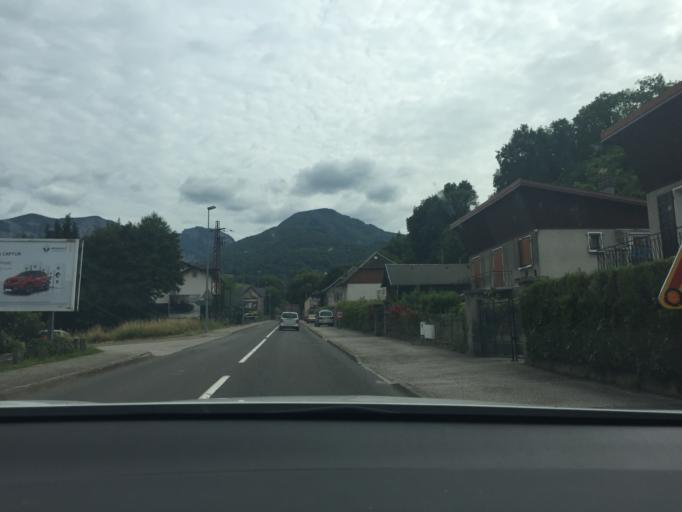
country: FR
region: Rhone-Alpes
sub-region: Departement de la Savoie
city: Cognin
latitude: 45.5536
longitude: 5.8914
